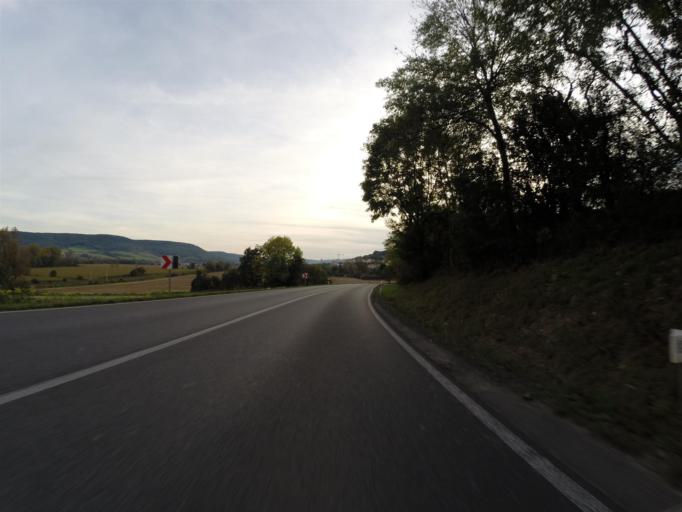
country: DE
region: Thuringia
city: Neuengonna
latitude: 50.9702
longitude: 11.6318
